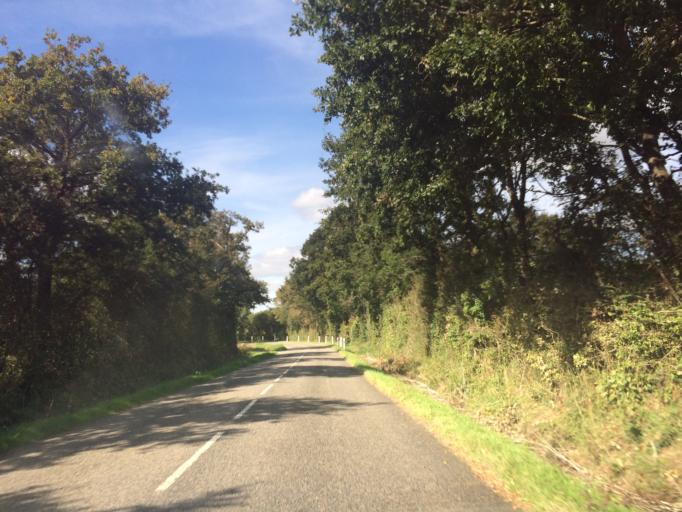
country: FR
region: Pays de la Loire
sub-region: Departement de la Loire-Atlantique
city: Chemere
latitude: 47.1142
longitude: -1.8982
